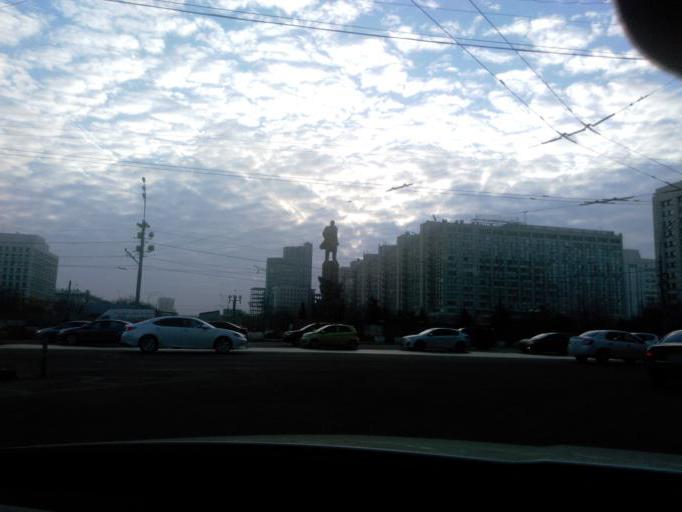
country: RU
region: Moscow
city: Zamoskvorech'ye
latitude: 55.7297
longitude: 37.6117
